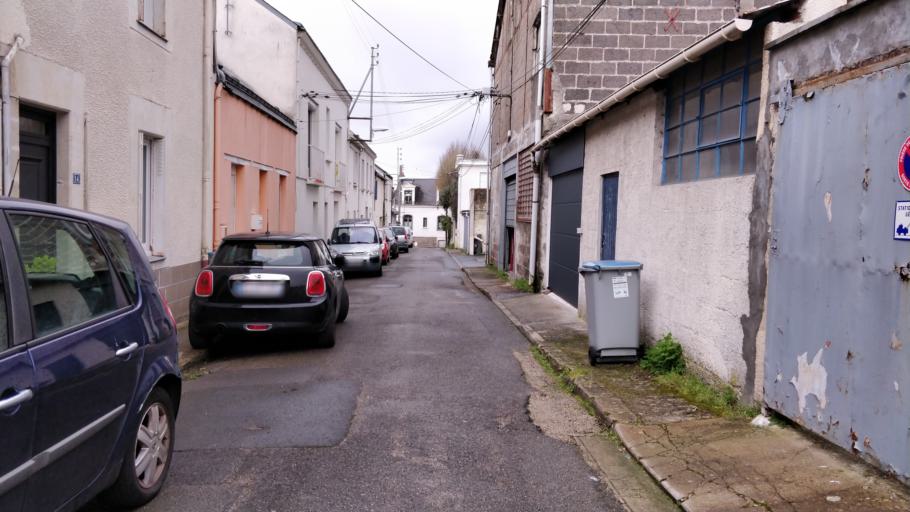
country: FR
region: Pays de la Loire
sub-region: Departement de la Loire-Atlantique
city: Nantes
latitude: 47.2340
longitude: -1.5402
